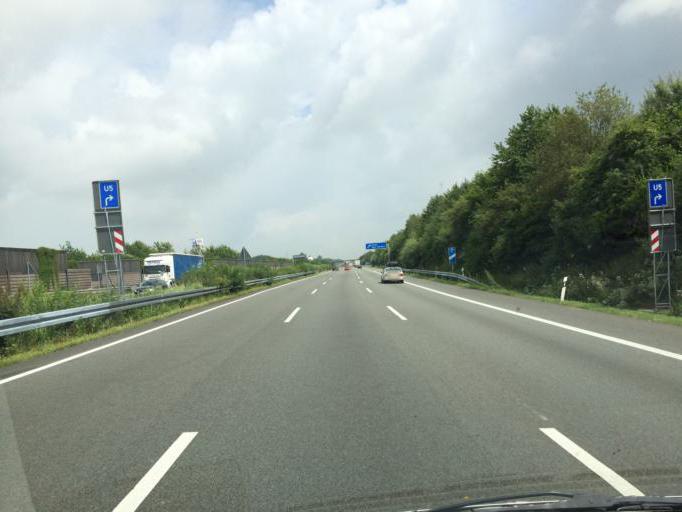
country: DE
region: Lower Saxony
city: Rehren
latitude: 52.2319
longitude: 9.2420
